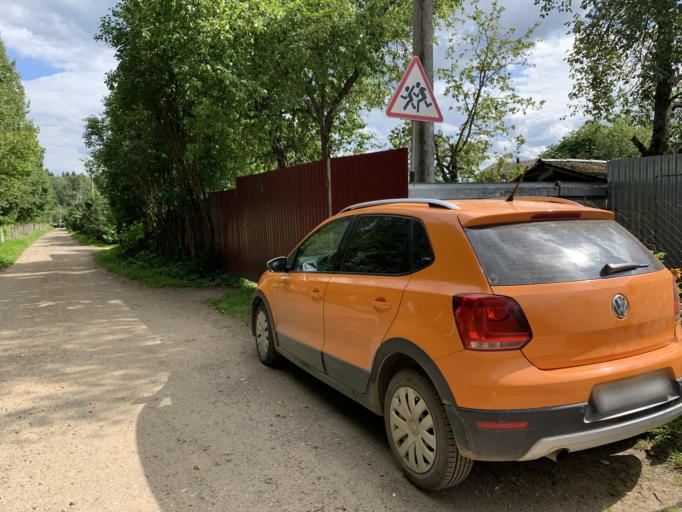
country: RU
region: Moskovskaya
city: Podosinki
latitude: 56.1805
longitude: 37.5773
